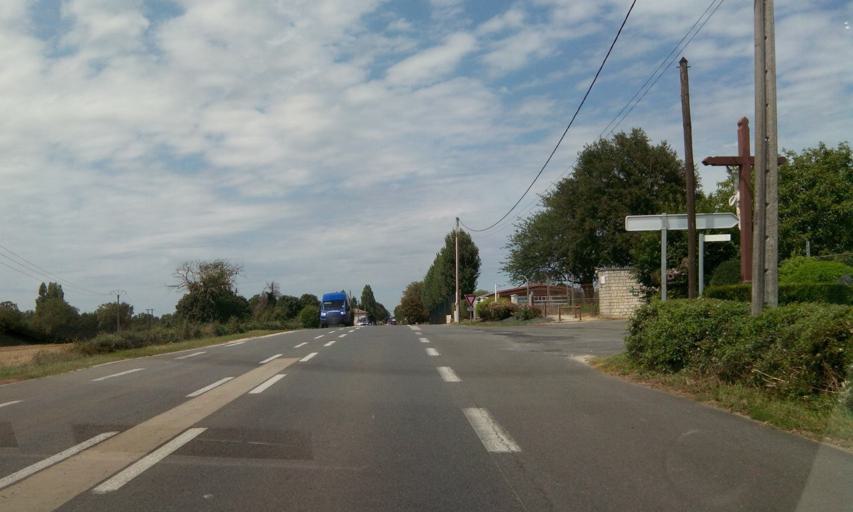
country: FR
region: Poitou-Charentes
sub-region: Departement des Deux-Sevres
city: Chef-Boutonne
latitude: 46.1907
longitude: -0.0544
